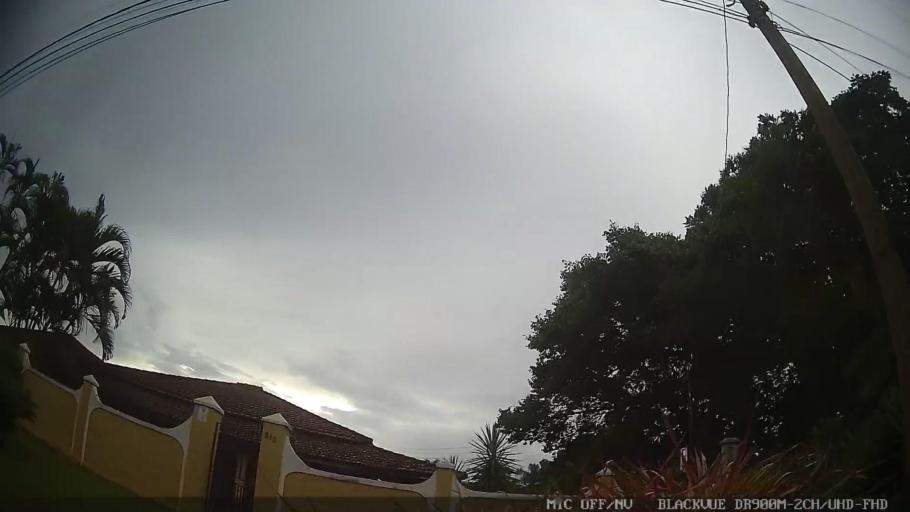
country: BR
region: Sao Paulo
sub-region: Jaguariuna
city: Jaguariuna
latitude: -22.7501
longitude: -47.0009
